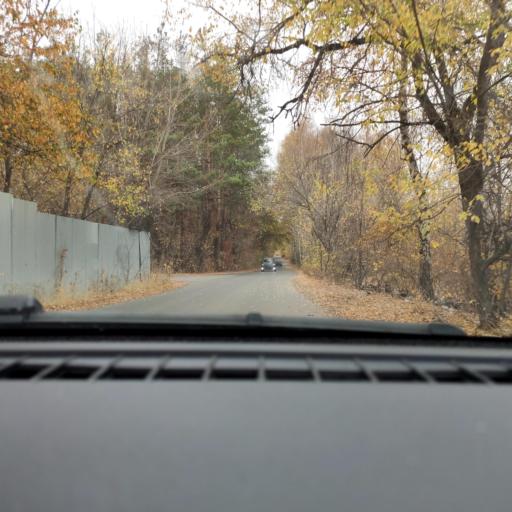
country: RU
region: Voronezj
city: Somovo
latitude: 51.6834
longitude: 39.2985
